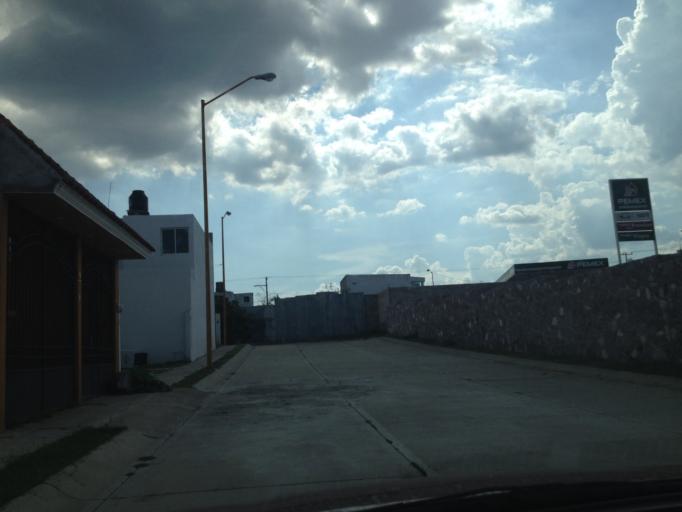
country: MX
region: Aguascalientes
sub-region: Aguascalientes
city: La Loma de los Negritos
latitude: 21.8478
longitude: -102.3415
